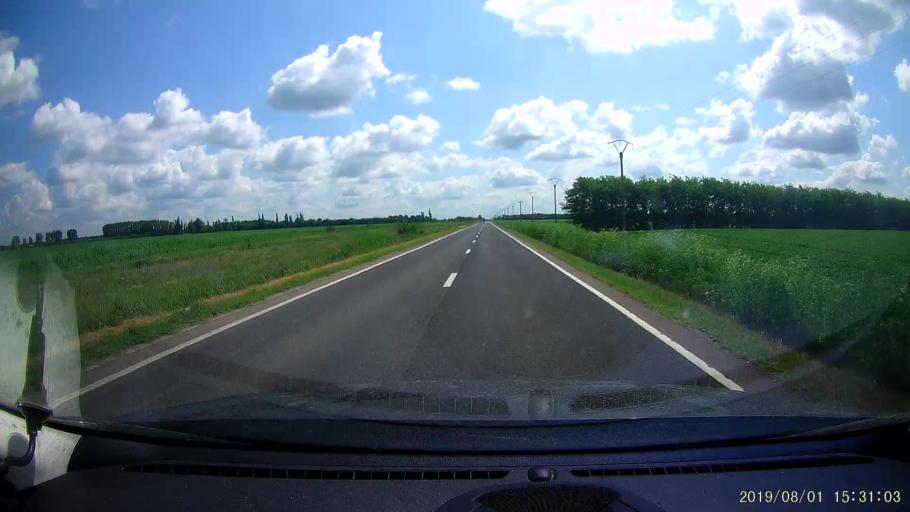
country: RO
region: Braila
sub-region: Comuna Stancuta
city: Cuza Voda
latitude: 44.9518
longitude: 27.6653
